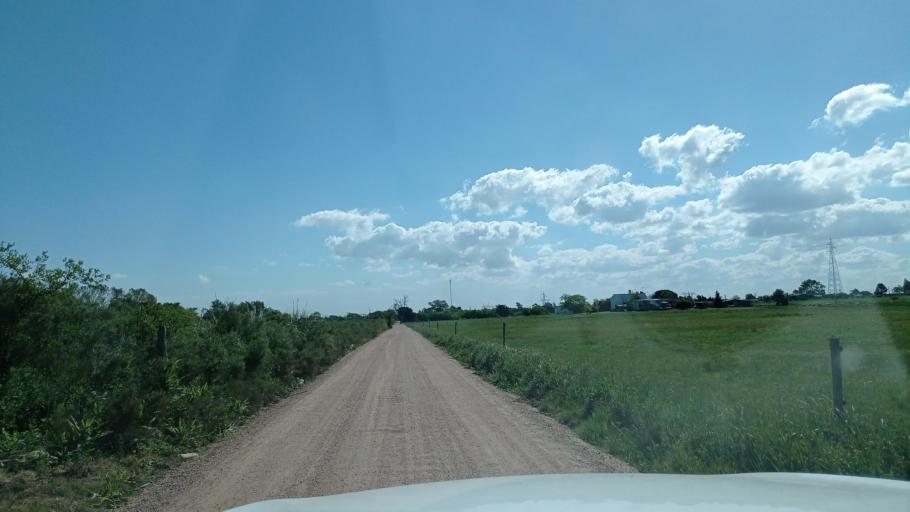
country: UY
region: Canelones
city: La Paz
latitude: -34.7827
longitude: -56.1626
